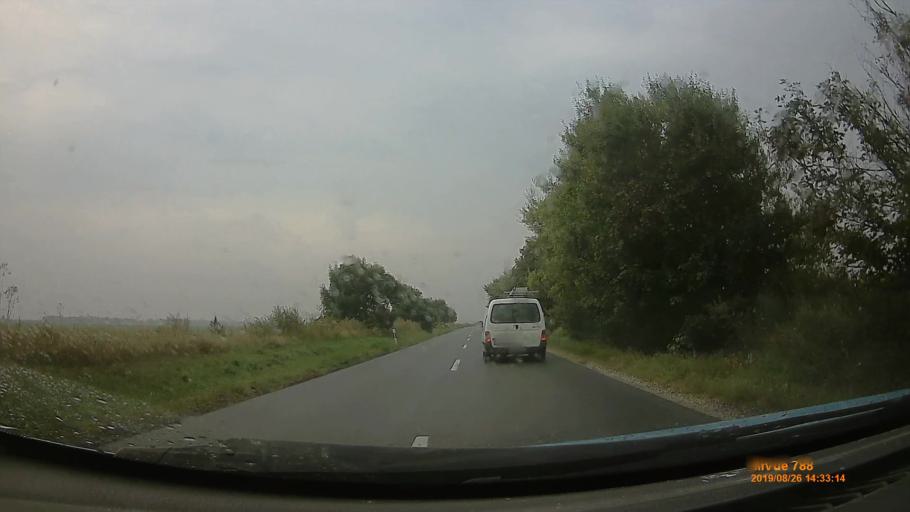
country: HU
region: Fejer
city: Zamoly
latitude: 47.2753
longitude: 18.4200
